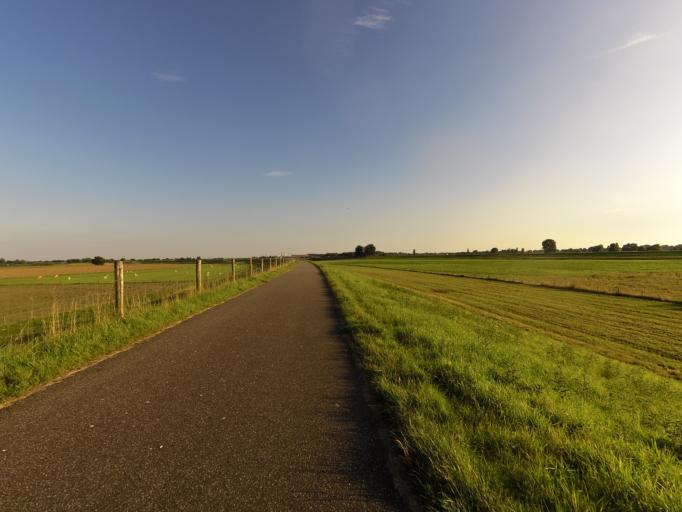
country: NL
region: Gelderland
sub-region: Gemeente Westervoort
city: Westervoort
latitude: 51.9569
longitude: 5.9547
